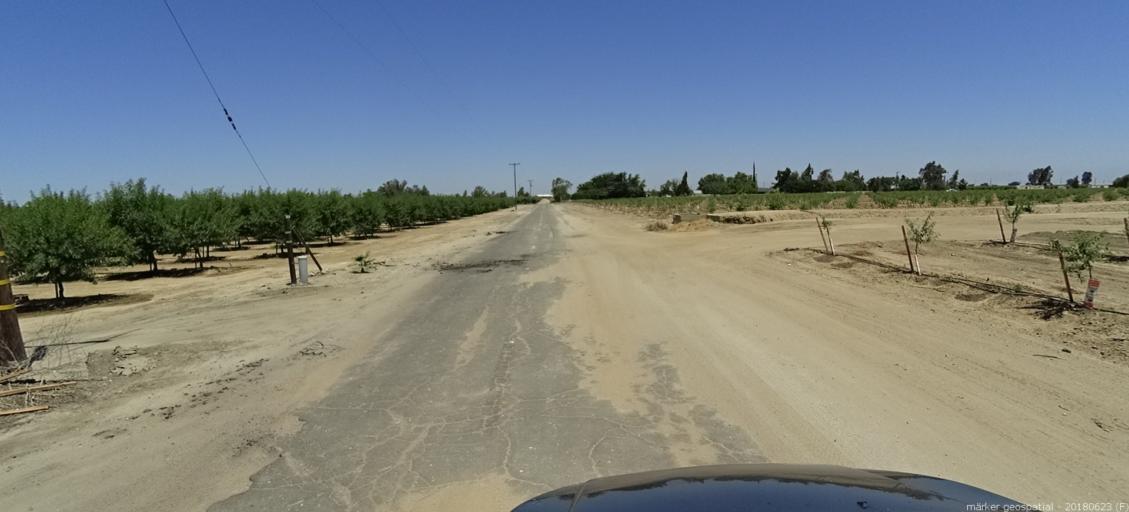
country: US
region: California
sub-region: Madera County
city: Chowchilla
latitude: 37.0963
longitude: -120.2385
